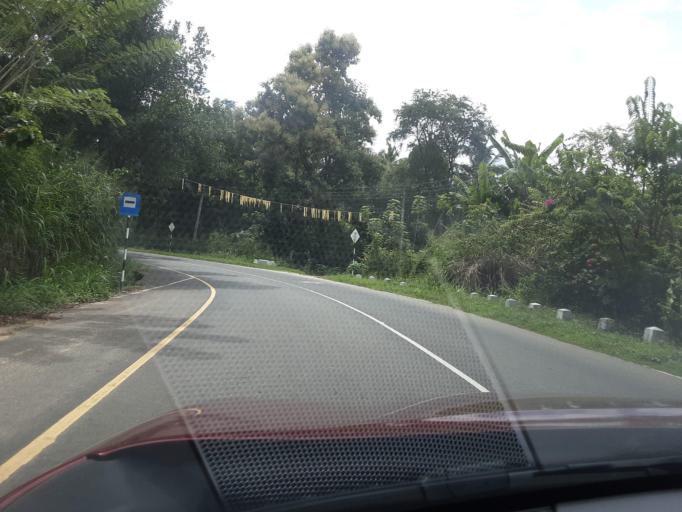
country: LK
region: Uva
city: Monaragala
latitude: 6.8984
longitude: 81.2843
